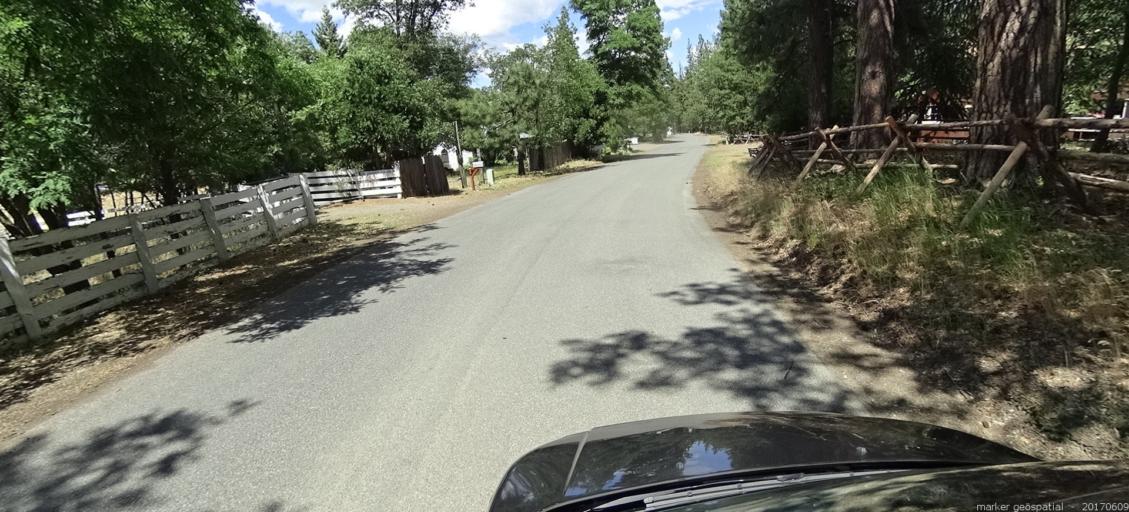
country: US
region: California
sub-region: Siskiyou County
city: Yreka
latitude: 41.4399
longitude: -122.9062
